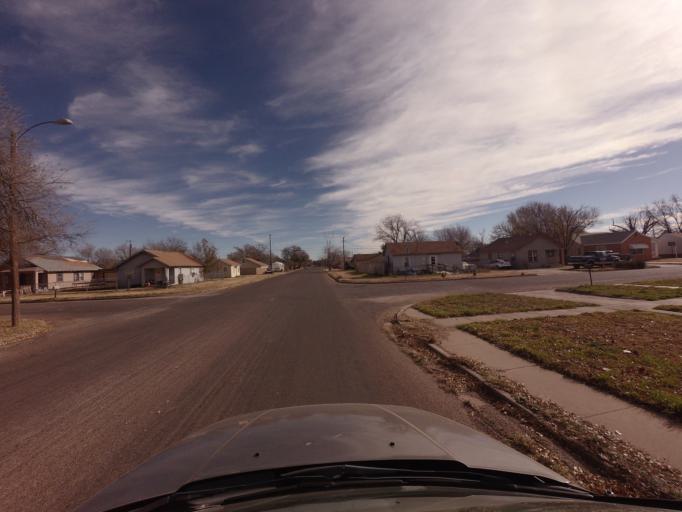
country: US
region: New Mexico
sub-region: Curry County
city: Clovis
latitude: 34.4078
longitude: -103.1992
